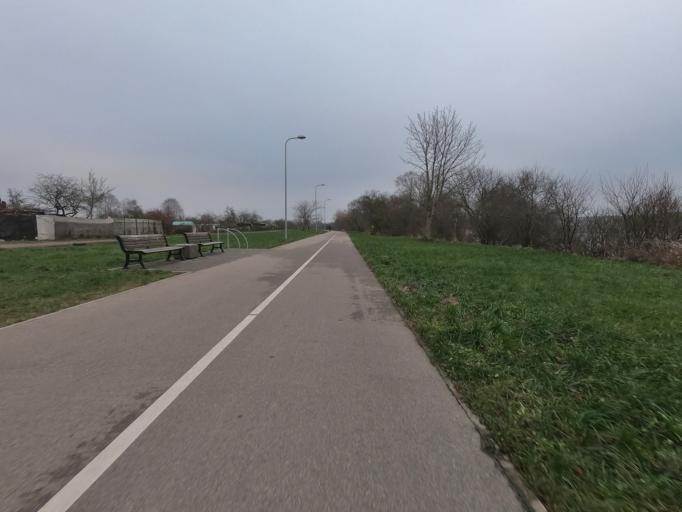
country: LV
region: Kekava
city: Kekava
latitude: 56.8813
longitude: 24.2153
